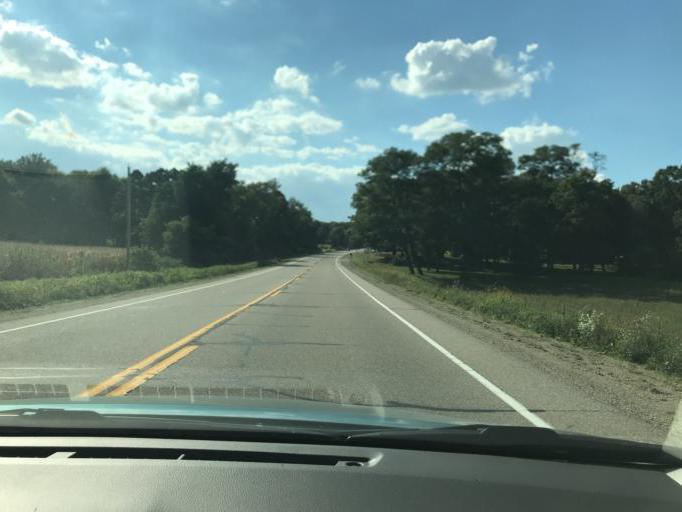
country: US
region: Wisconsin
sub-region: Rock County
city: Orfordville
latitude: 42.5257
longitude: -89.2165
